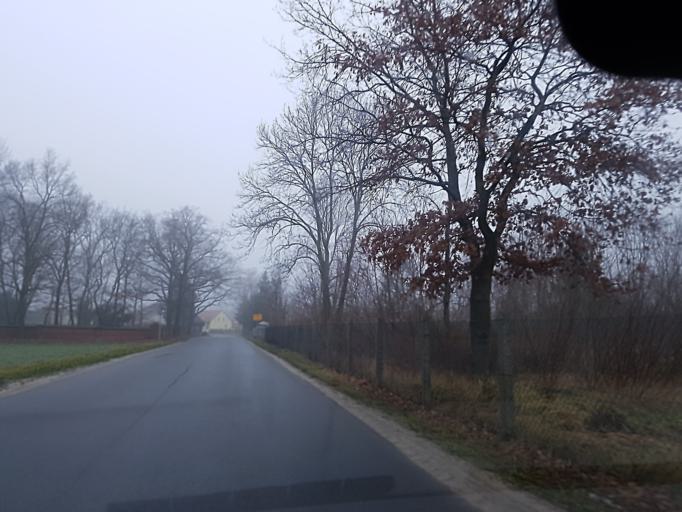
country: DE
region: Brandenburg
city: Finsterwalde
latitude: 51.6397
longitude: 13.7399
